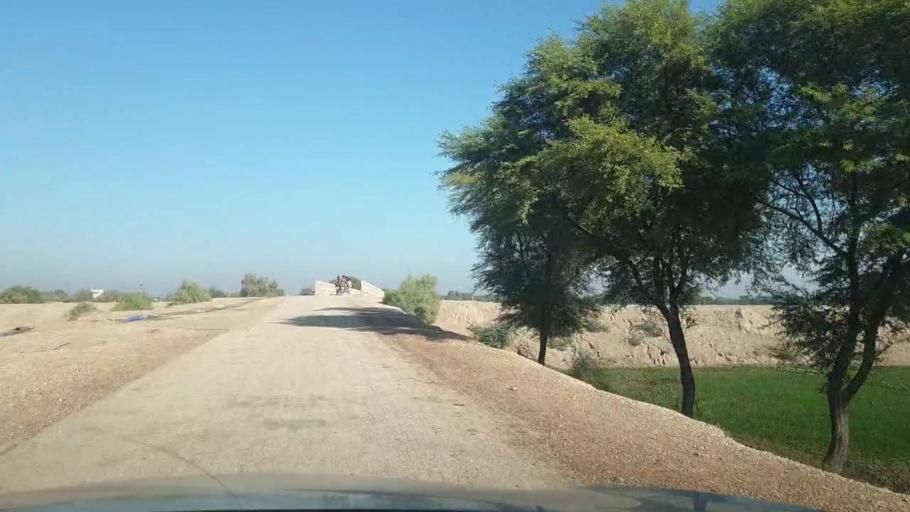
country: PK
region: Sindh
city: Bhan
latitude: 26.5578
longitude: 67.6640
